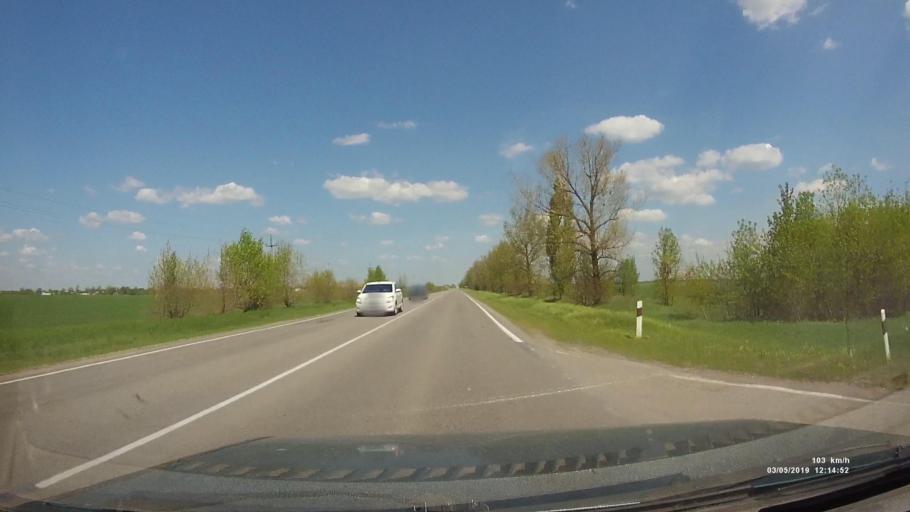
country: RU
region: Rostov
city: Melikhovskaya
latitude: 47.3500
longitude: 40.5679
